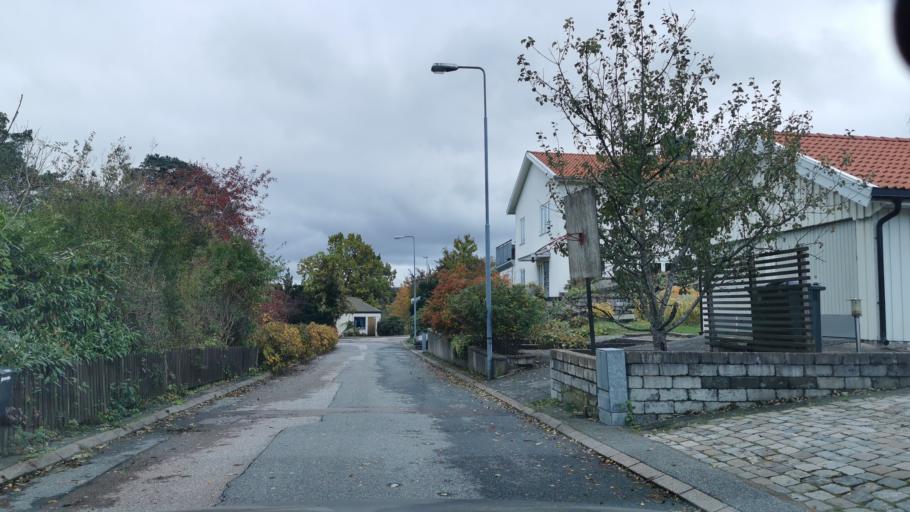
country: SE
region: Vaestra Goetaland
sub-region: Partille Kommun
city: Partille
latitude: 57.7252
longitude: 12.0726
